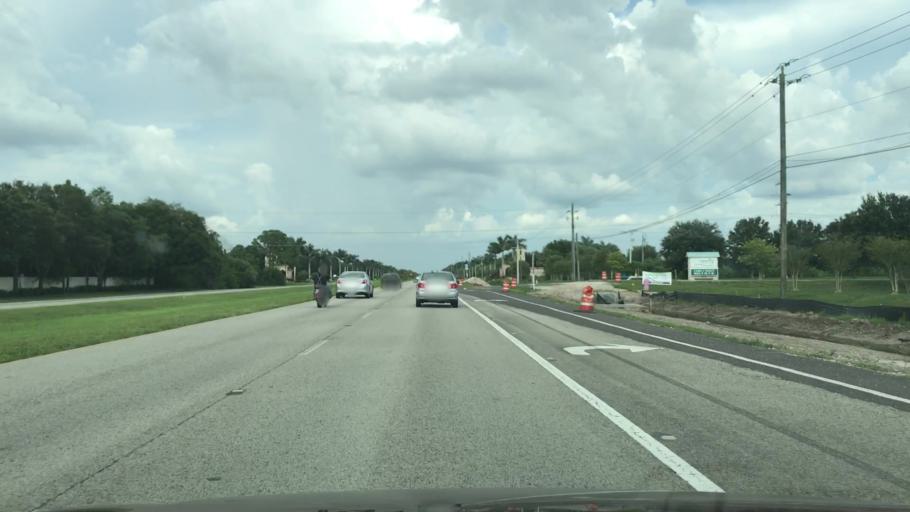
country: US
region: Florida
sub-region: Sarasota County
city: Plantation
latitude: 27.0495
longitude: -82.3542
